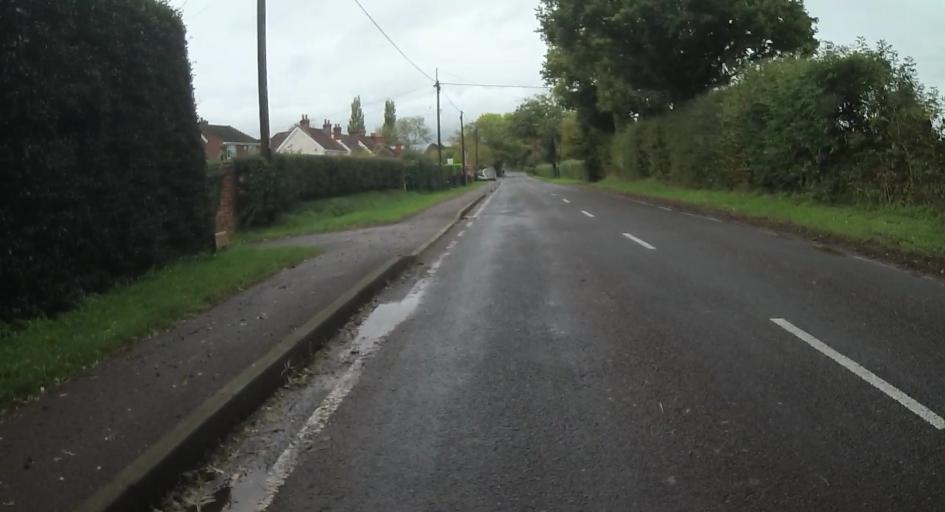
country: GB
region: England
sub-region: Hampshire
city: Tadley
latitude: 51.3480
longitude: -1.1646
